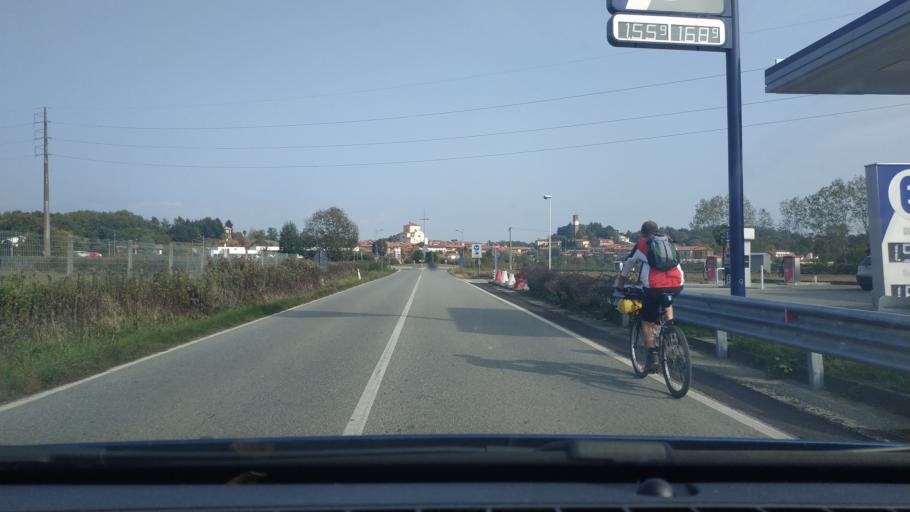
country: IT
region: Piedmont
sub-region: Provincia di Torino
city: Romano Canavese
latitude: 45.3845
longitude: 7.8616
